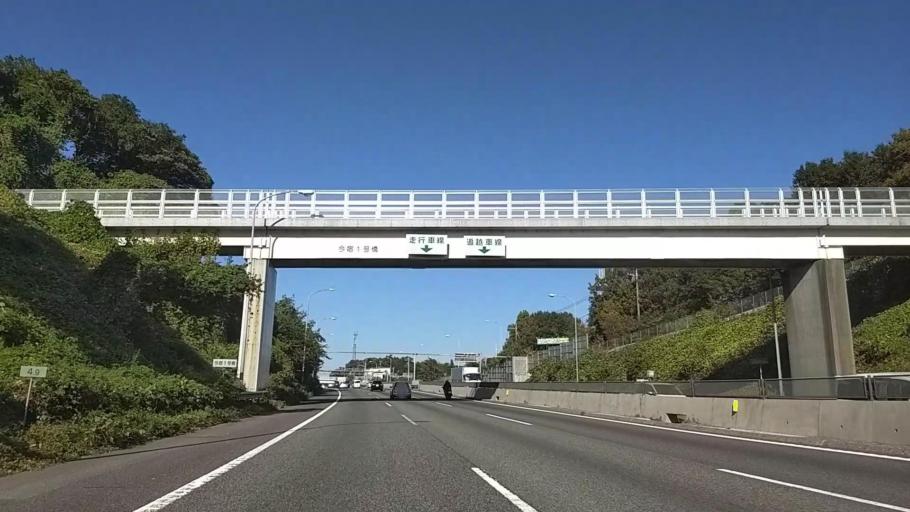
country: JP
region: Kanagawa
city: Minami-rinkan
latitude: 35.4766
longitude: 139.5261
